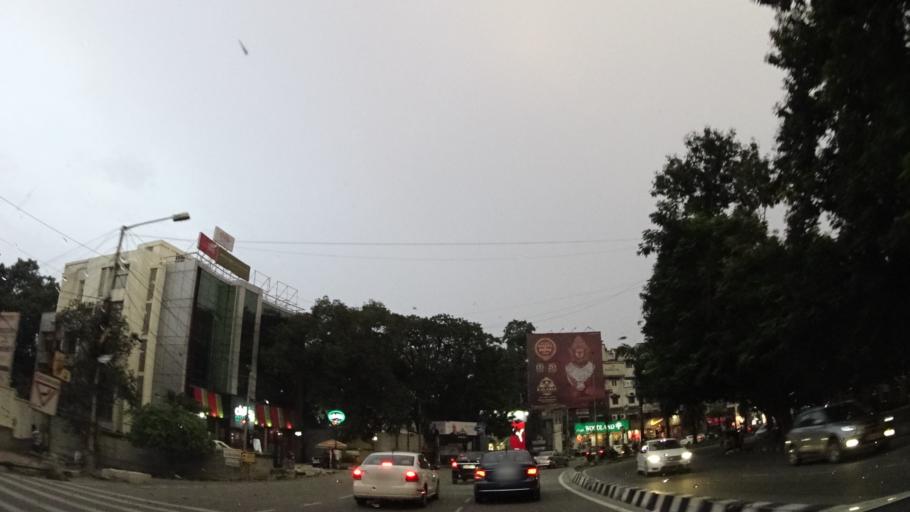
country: IN
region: Telangana
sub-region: Hyderabad
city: Hyderabad
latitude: 17.4230
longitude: 78.4492
